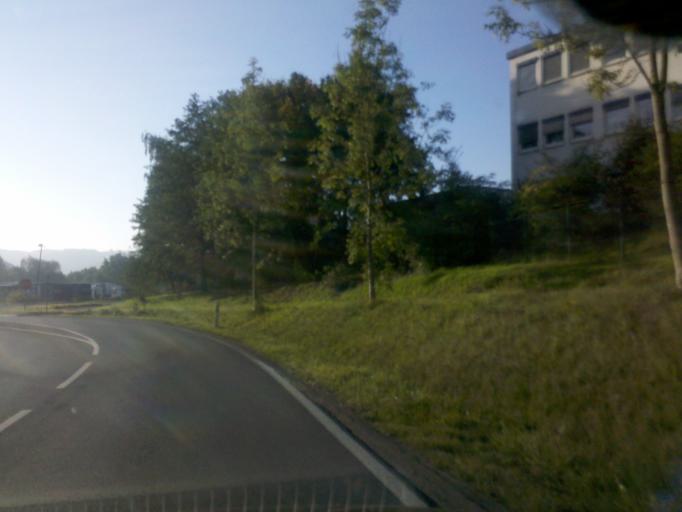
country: DE
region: Hesse
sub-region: Regierungsbezirk Giessen
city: Haiger
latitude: 50.7543
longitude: 8.2063
